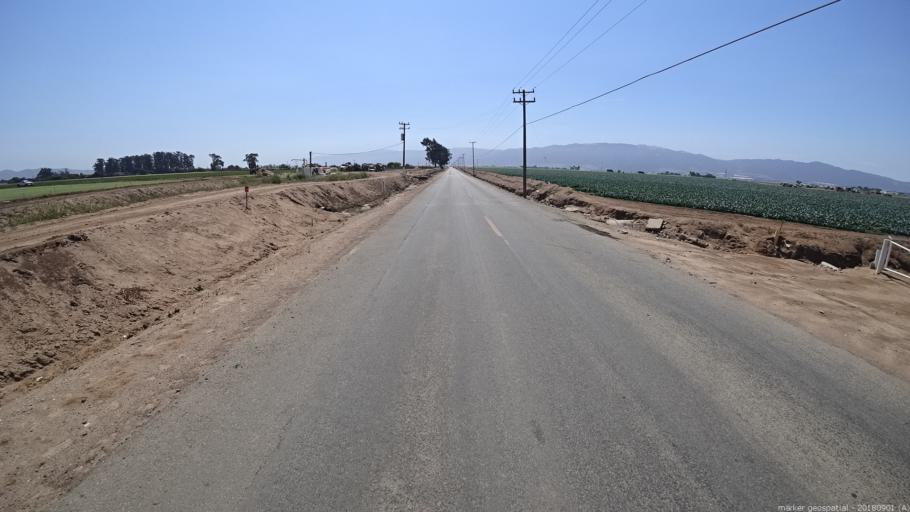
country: US
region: California
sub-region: Monterey County
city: Chualar
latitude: 36.6478
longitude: -121.5424
